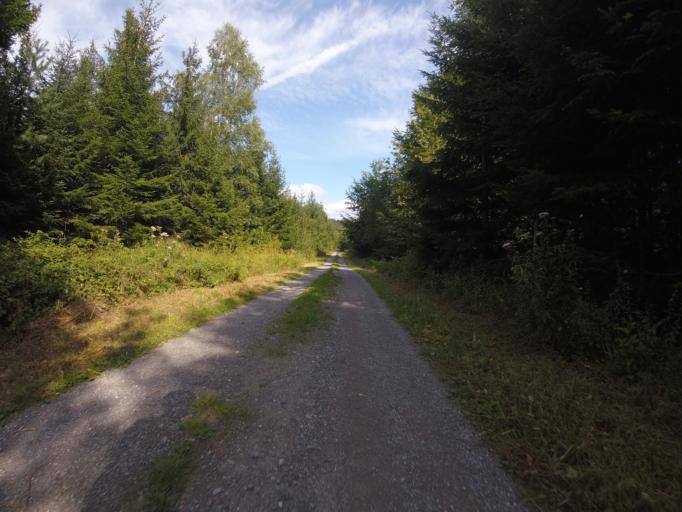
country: DE
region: Baden-Wuerttemberg
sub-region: Regierungsbezirk Stuttgart
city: Sulzbach an der Murr
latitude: 48.9726
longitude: 9.5126
